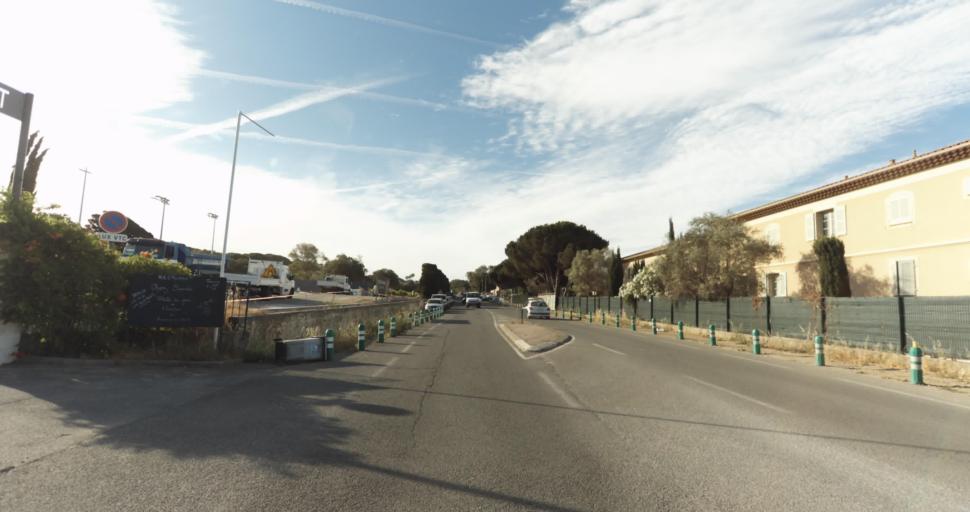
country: FR
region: Provence-Alpes-Cote d'Azur
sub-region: Departement du Var
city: Saint-Tropez
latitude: 43.2589
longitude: 6.6324
